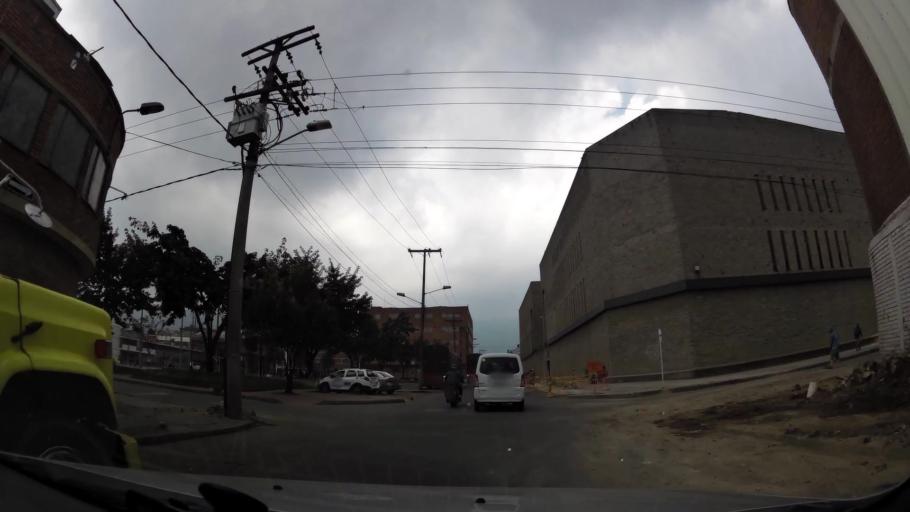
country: CO
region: Bogota D.C.
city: Bogota
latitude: 4.6206
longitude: -74.0939
